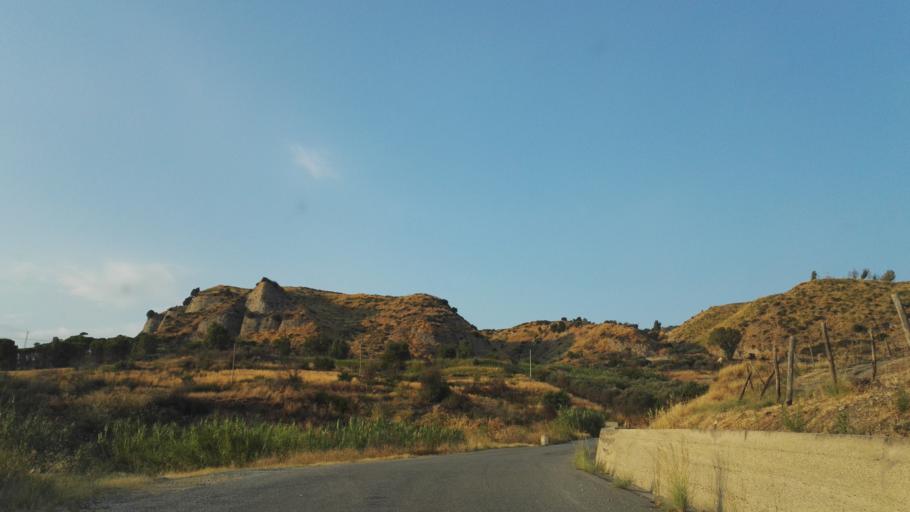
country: IT
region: Calabria
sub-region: Provincia di Reggio Calabria
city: Caulonia
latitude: 38.3940
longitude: 16.4287
